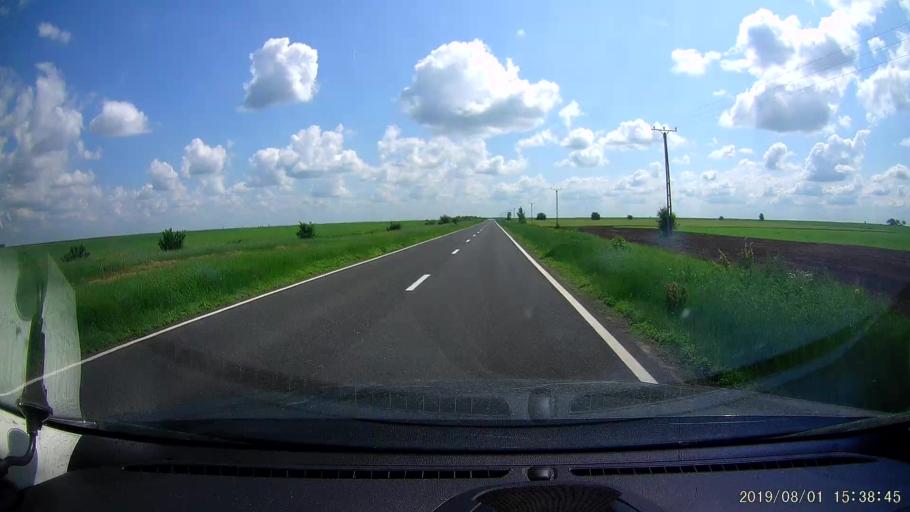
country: RO
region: Braila
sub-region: Comuna Insuratei
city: Insuratei
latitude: 44.8740
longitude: 27.5714
